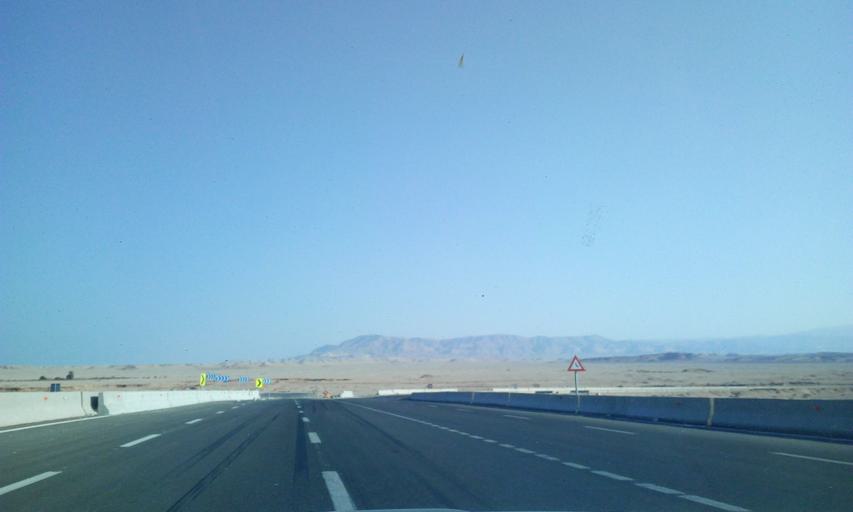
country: EG
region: As Suways
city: Ain Sukhna
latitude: 29.1081
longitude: 32.5336
